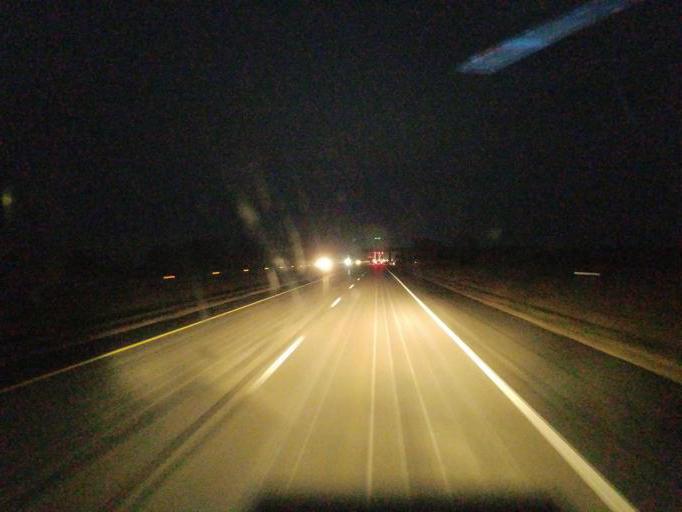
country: US
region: Iowa
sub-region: Guthrie County
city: Stuart
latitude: 41.4959
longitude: -94.3790
